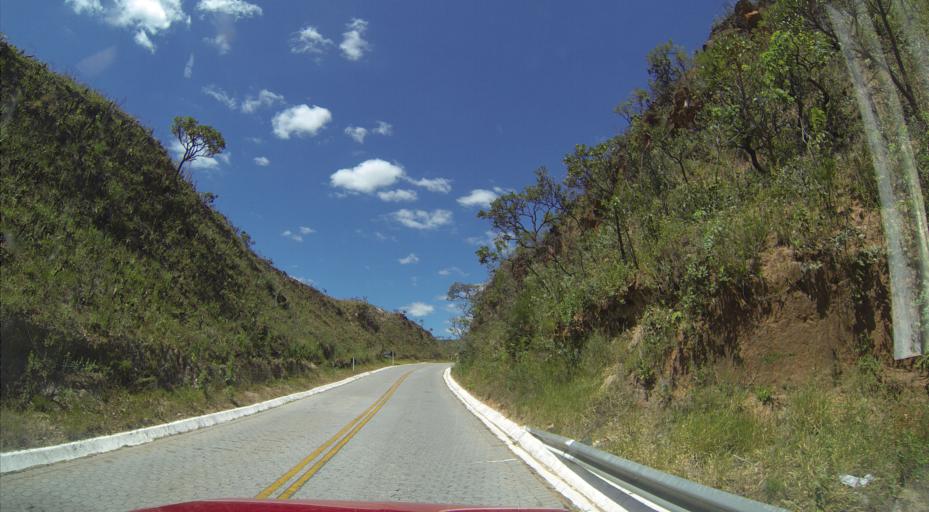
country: BR
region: Minas Gerais
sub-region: Conceicao Do Mato Dentro
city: Conceicao do Mato Dentro
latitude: -19.3065
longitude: -43.6075
